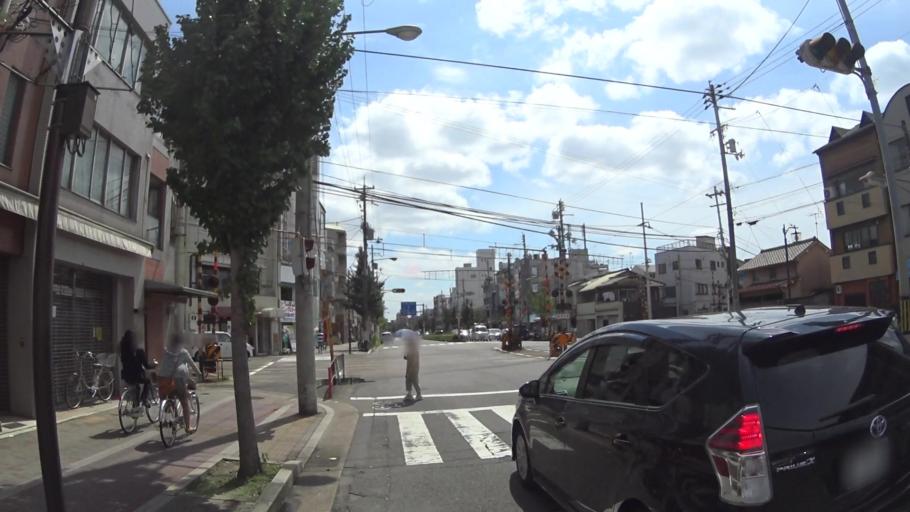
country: JP
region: Kyoto
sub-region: Kyoto-shi
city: Kamigyo-ku
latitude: 35.0353
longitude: 135.7812
